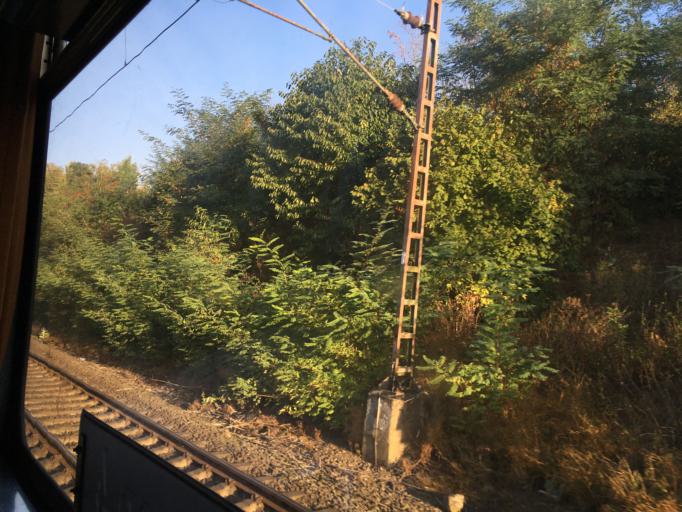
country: DE
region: North Rhine-Westphalia
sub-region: Regierungsbezirk Arnsberg
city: Dortmund
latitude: 51.4894
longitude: 7.4893
